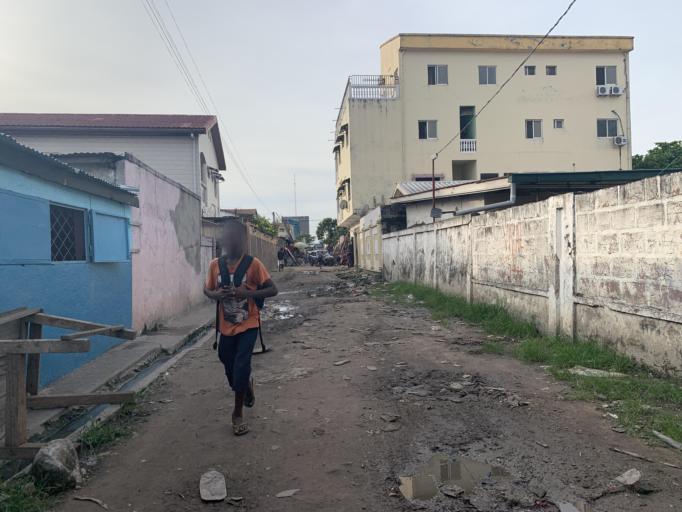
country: CG
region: Brazzaville
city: Brazzaville
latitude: -4.2492
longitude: 15.2832
